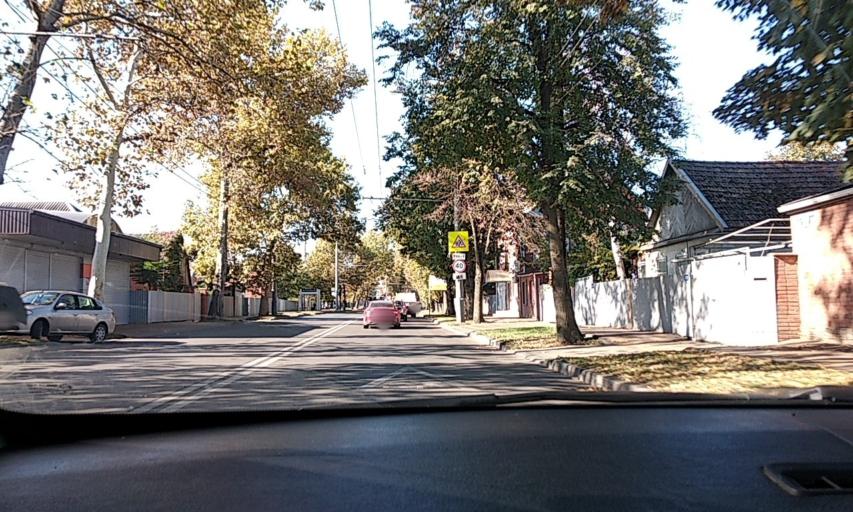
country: RU
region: Krasnodarskiy
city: Pashkovskiy
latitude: 45.0192
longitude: 39.1025
